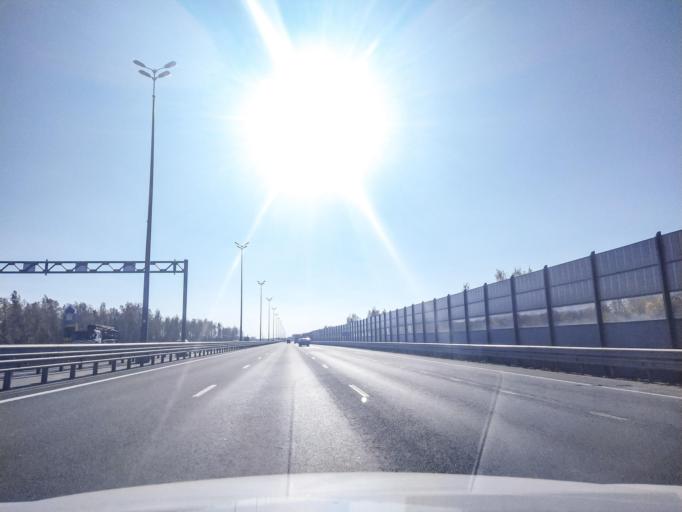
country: RU
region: Leningrad
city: Gatchina
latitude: 59.5721
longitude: 30.1695
